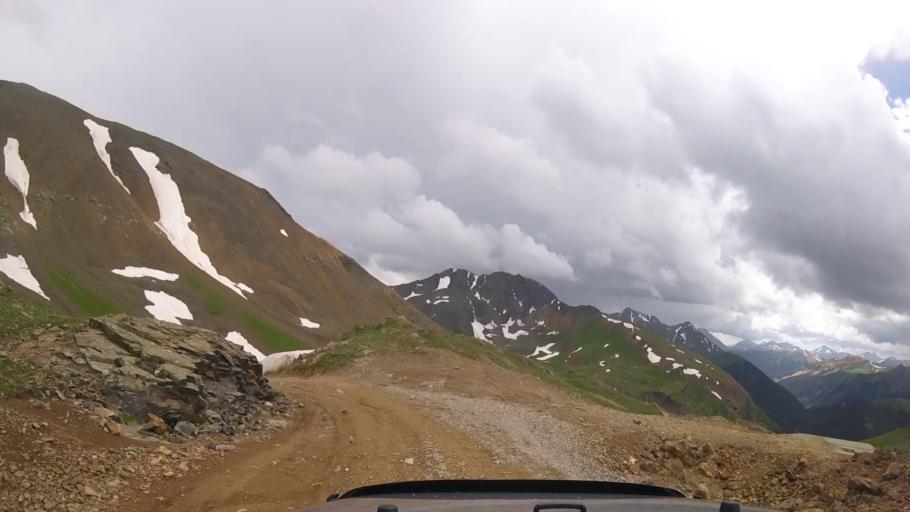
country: US
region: Colorado
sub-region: San Juan County
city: Silverton
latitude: 37.9169
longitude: -107.6283
